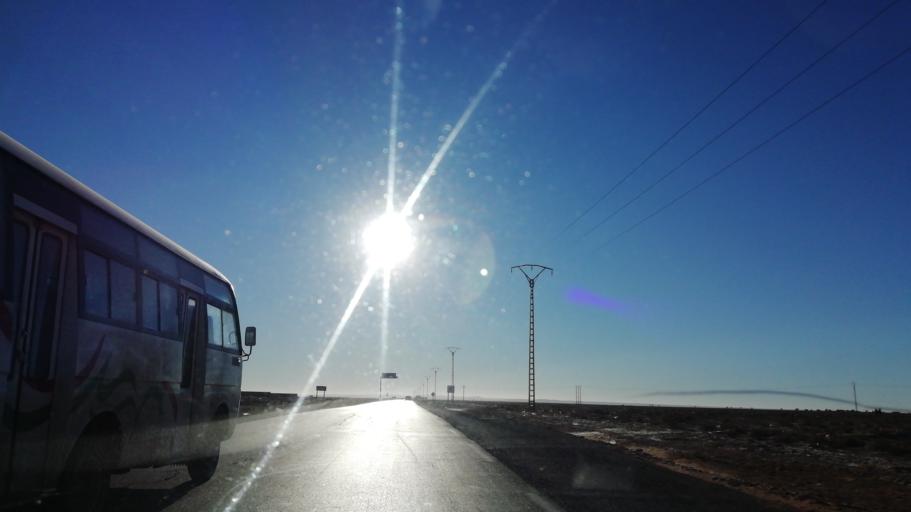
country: DZ
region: Saida
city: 'Ain el Hadjar
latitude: 34.0217
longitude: 0.1028
